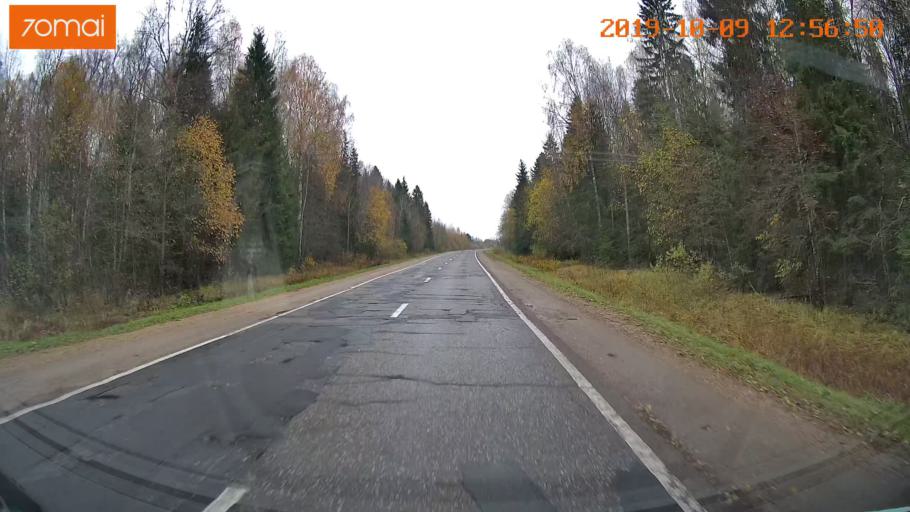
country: RU
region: Jaroslavl
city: Prechistoye
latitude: 58.3940
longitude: 40.4231
